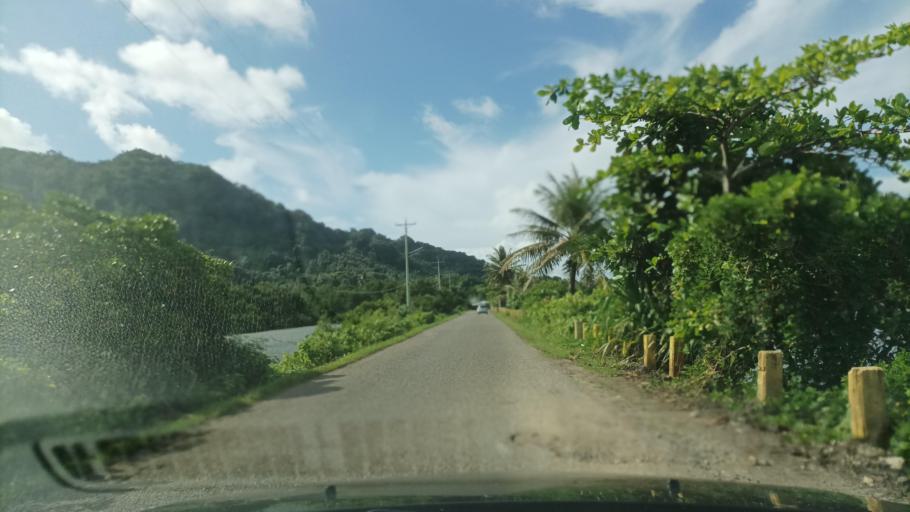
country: FM
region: Kosrae
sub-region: Lelu Municipality
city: Lelu
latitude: 5.3381
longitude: 163.0204
